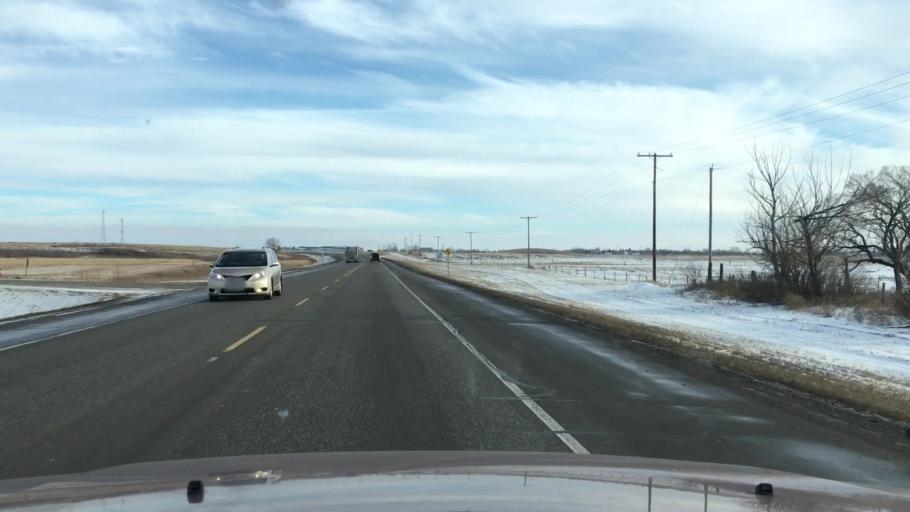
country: CA
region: Saskatchewan
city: Pilot Butte
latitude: 50.4844
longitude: -104.4468
